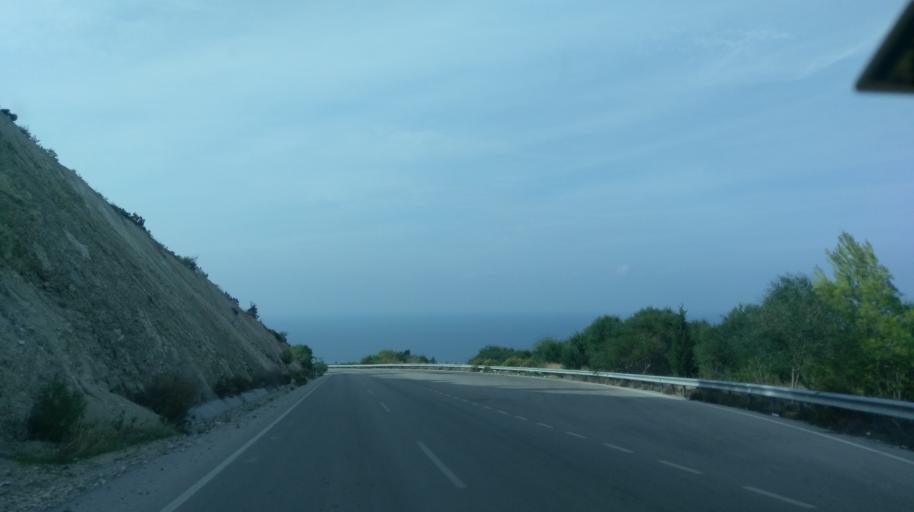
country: CY
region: Ammochostos
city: Trikomo
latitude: 35.4293
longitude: 33.9674
